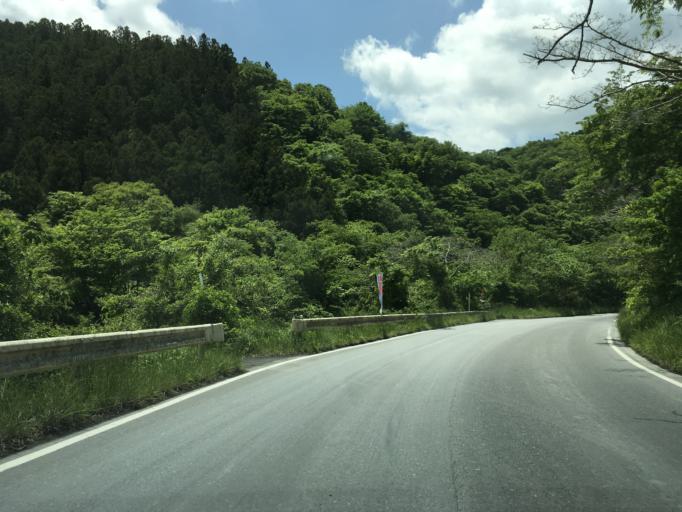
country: JP
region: Miyagi
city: Wakuya
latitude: 38.6580
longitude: 141.3221
